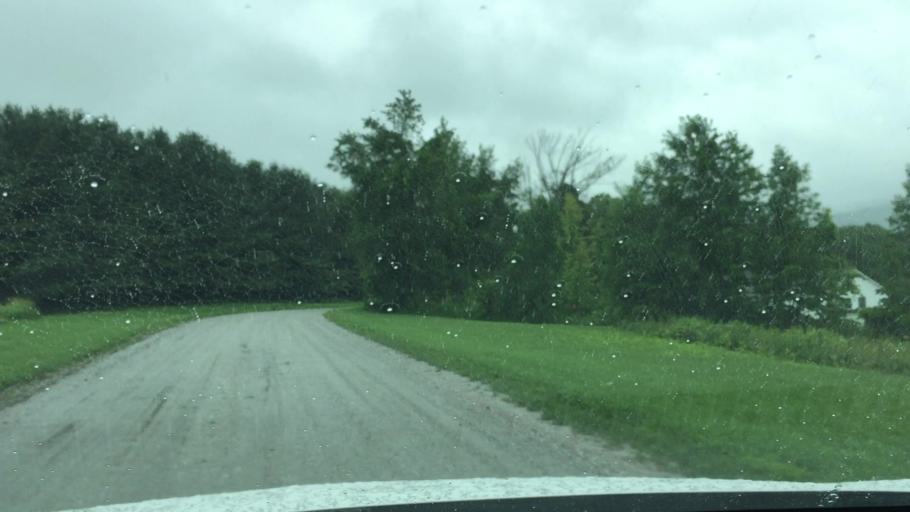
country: US
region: Massachusetts
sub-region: Berkshire County
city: Lanesborough
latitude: 42.5448
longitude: -73.2423
